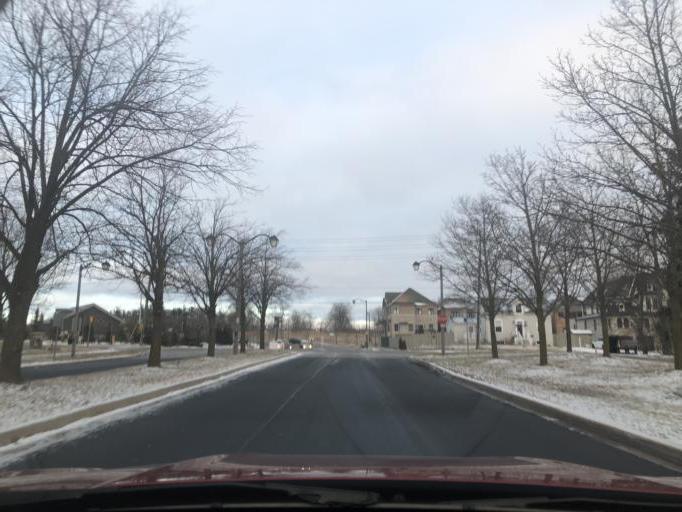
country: CA
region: Ontario
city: Markham
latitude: 43.8638
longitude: -79.2320
